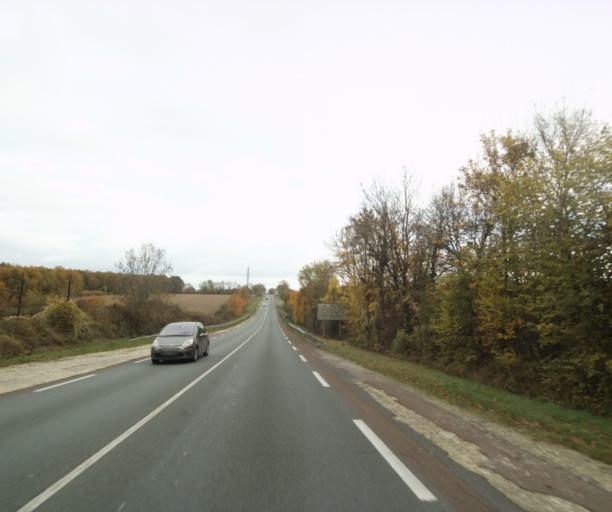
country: FR
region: Poitou-Charentes
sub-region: Departement de la Charente-Maritime
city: Saintes
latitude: 45.7599
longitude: -0.6662
